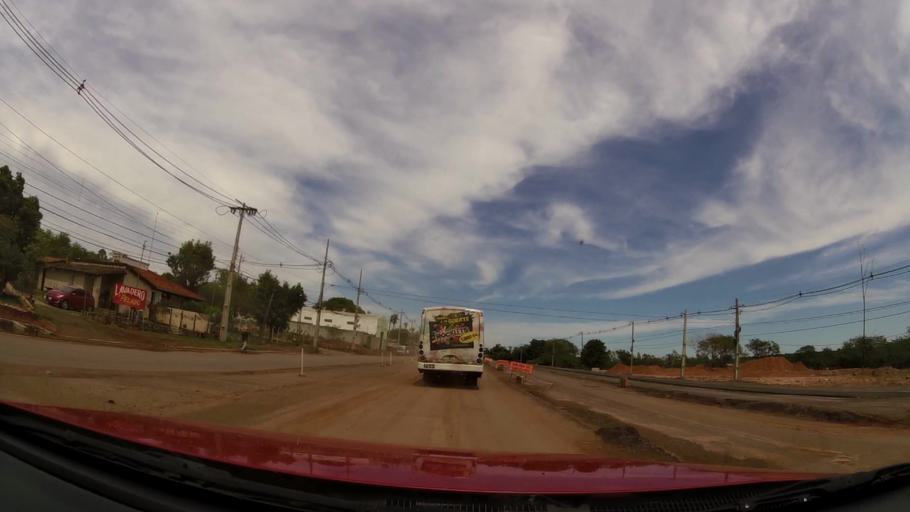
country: PY
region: Central
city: Limpio
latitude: -25.1930
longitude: -57.5067
